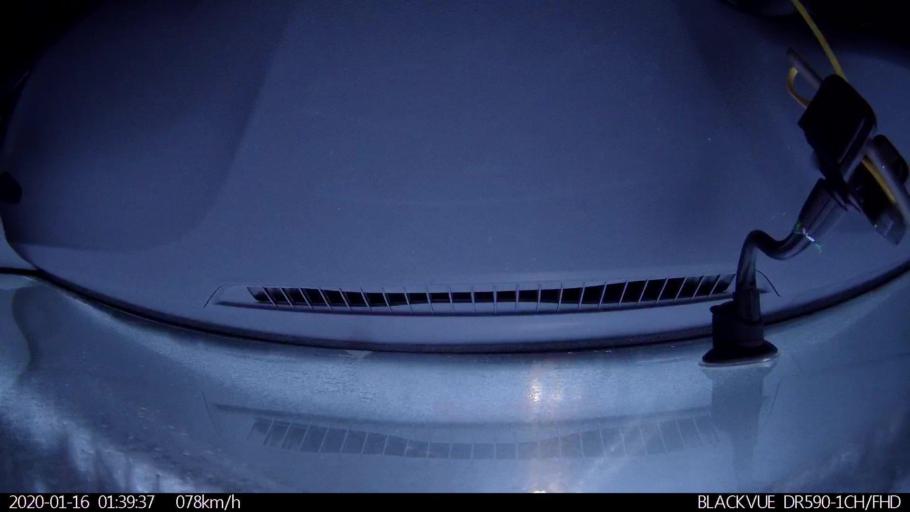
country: RU
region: Nizjnij Novgorod
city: Gorbatovka
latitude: 56.3332
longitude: 43.7929
